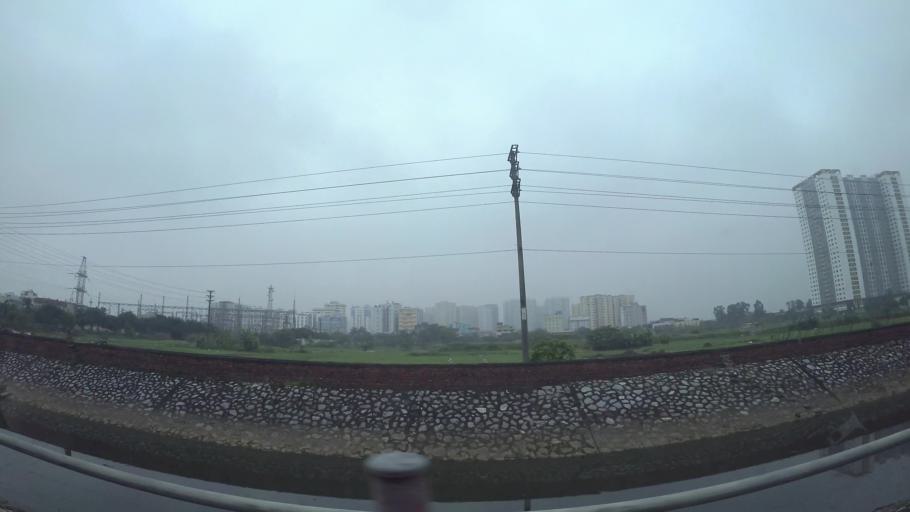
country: VN
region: Ha Noi
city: Hai BaTrung
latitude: 20.9796
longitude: 105.8685
